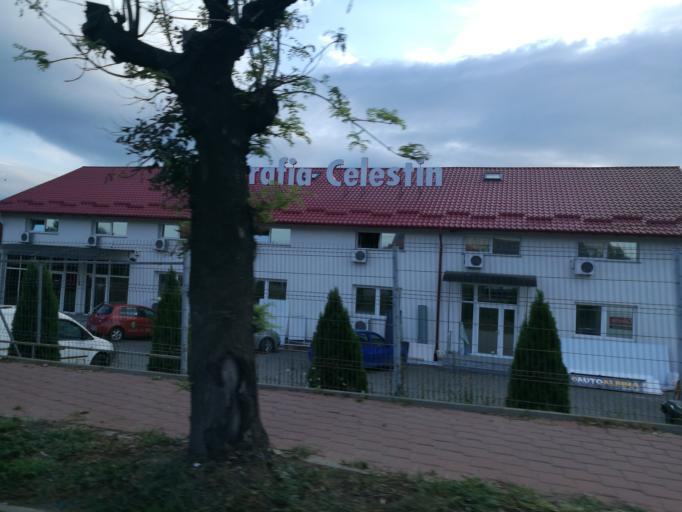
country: RO
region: Suceava
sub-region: Comuna Scheia
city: Scheia
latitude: 47.6808
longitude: 26.2359
